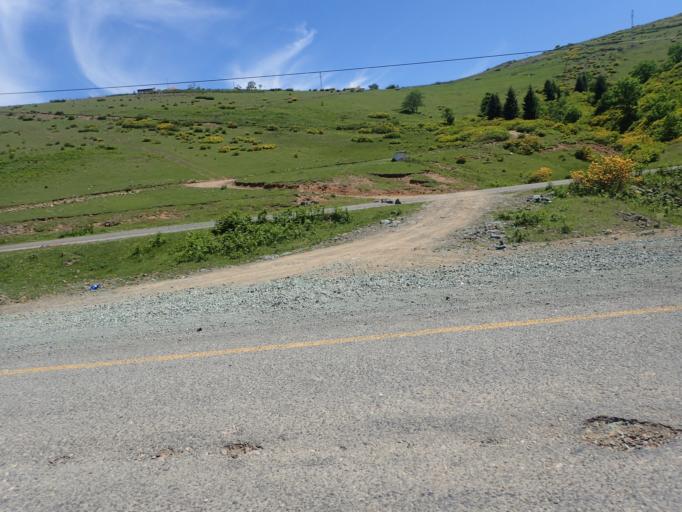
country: TR
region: Ordu
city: Topcam
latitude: 40.6716
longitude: 37.9318
